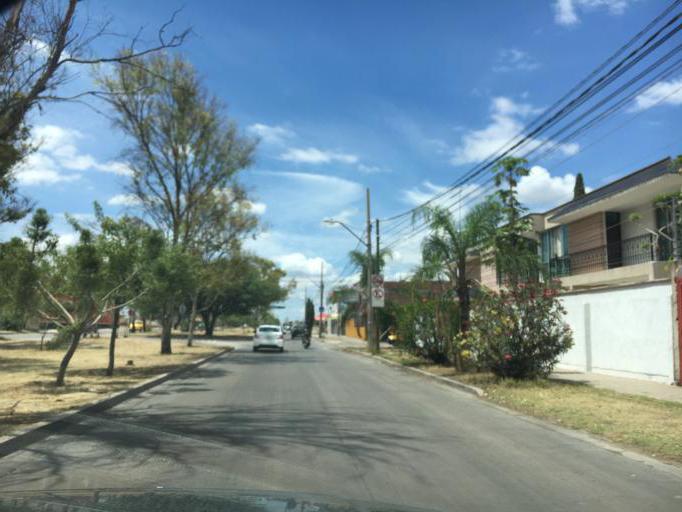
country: MX
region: Guanajuato
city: Leon
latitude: 21.0954
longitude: -101.6417
